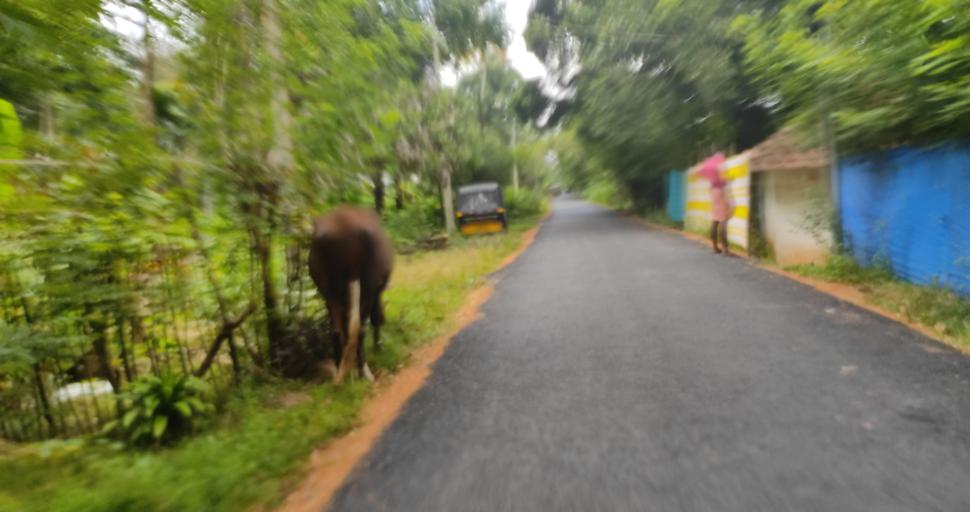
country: IN
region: Kerala
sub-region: Alappuzha
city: Shertallai
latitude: 9.6639
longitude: 76.3321
